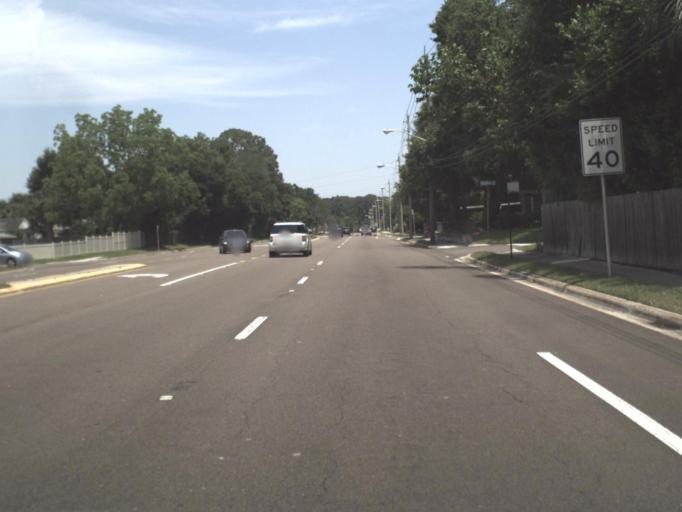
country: US
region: Florida
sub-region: Duval County
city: Jacksonville
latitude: 30.2767
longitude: -81.6503
